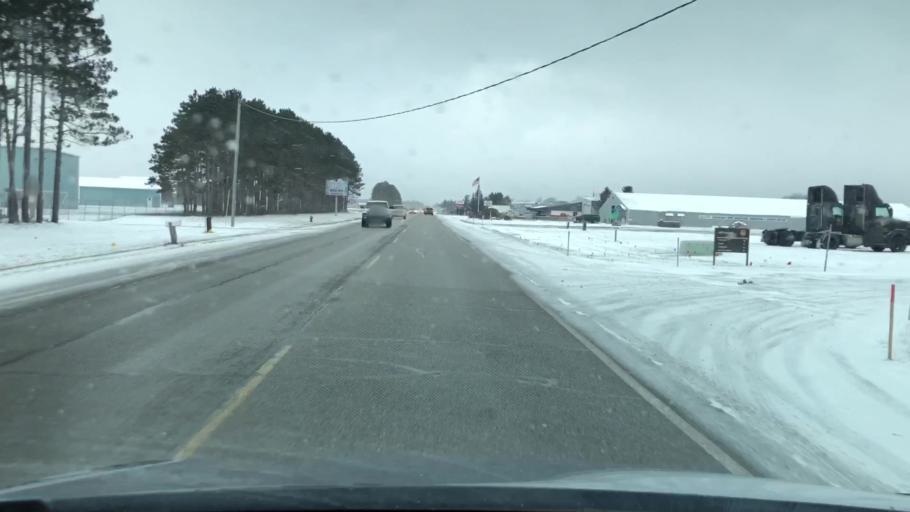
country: US
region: Michigan
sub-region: Wexford County
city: Cadillac
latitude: 44.2813
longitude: -85.4137
